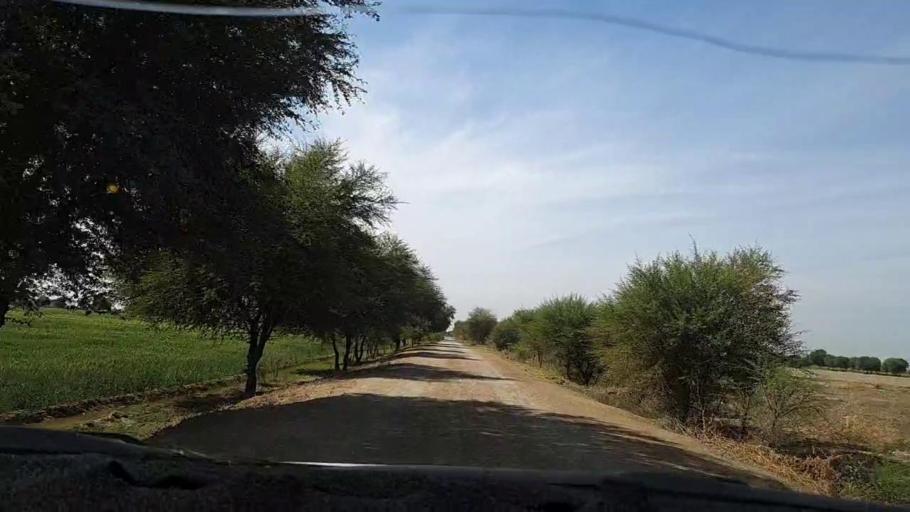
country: PK
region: Sindh
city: Pithoro
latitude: 25.5018
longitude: 69.4693
